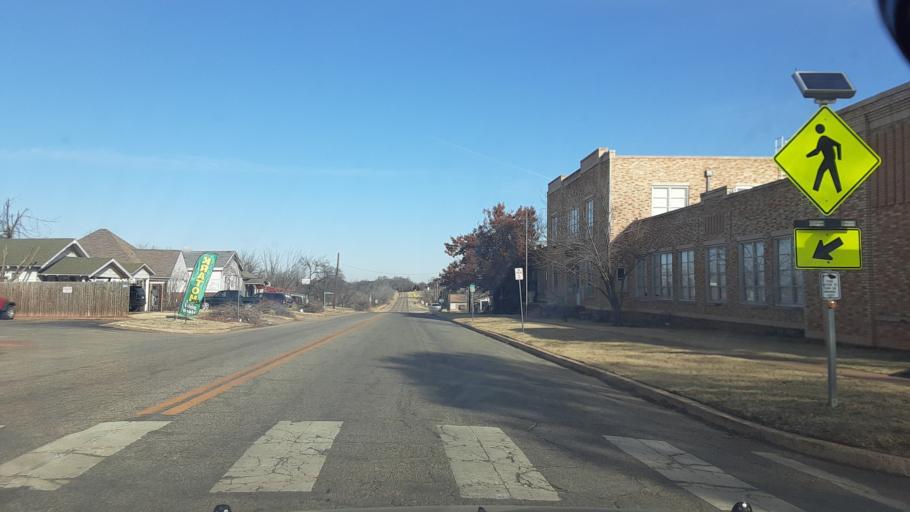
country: US
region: Oklahoma
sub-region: Logan County
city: Guthrie
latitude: 35.8864
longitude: -97.4240
